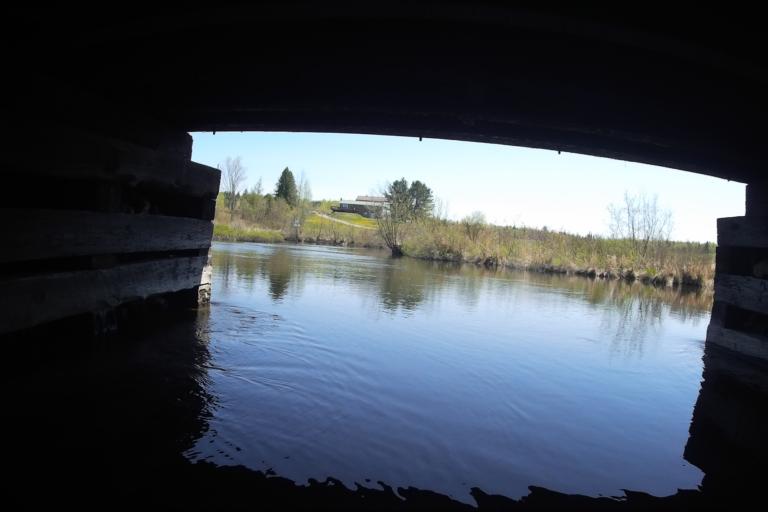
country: CA
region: Ontario
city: Powassan
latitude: 46.1558
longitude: -79.2476
